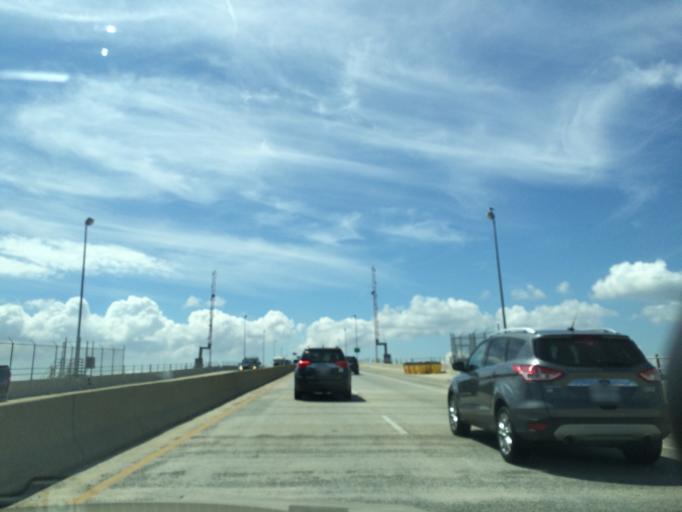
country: US
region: Virginia
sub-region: York County
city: Yorktown
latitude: 37.2446
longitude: -76.5054
